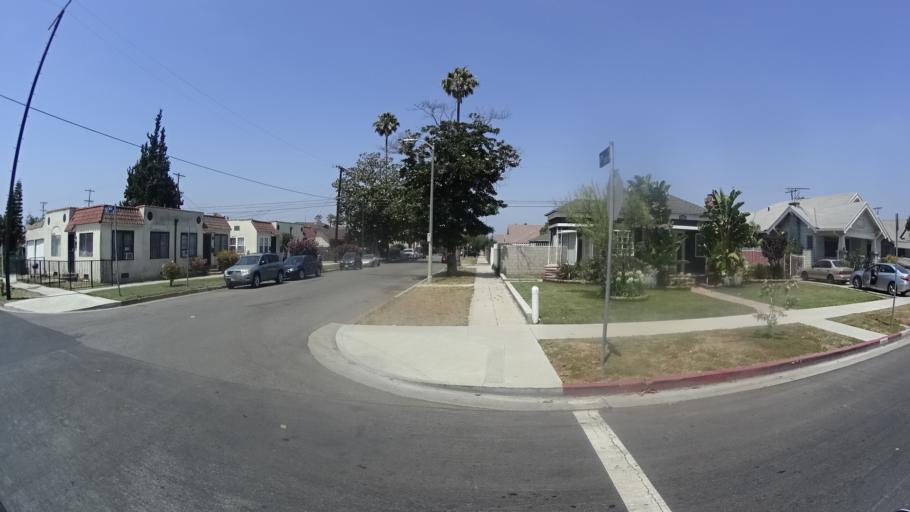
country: US
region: California
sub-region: Los Angeles County
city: View Park-Windsor Hills
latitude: 34.0203
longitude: -118.3166
